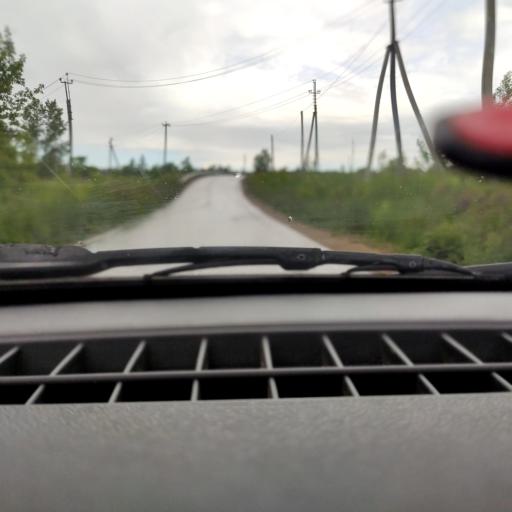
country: RU
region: Bashkortostan
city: Kabakovo
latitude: 54.5657
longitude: 56.2709
